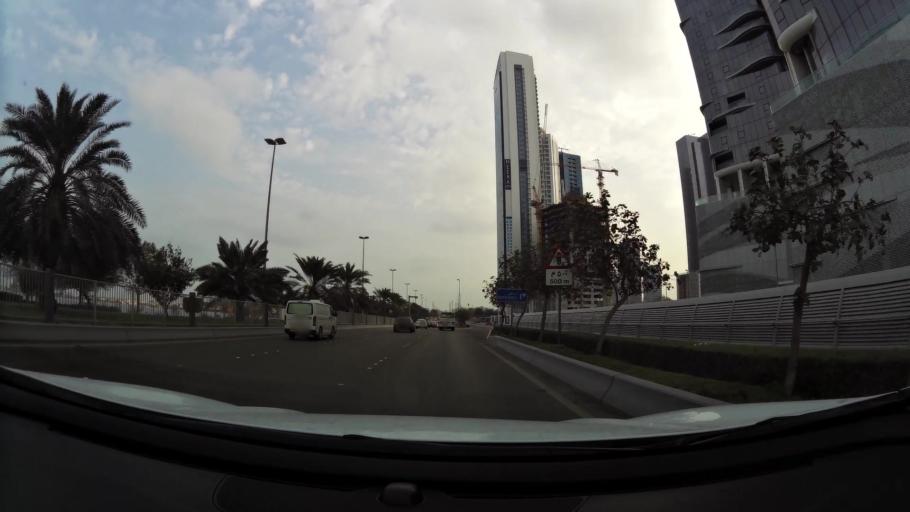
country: AE
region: Abu Dhabi
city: Abu Dhabi
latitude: 24.5023
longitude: 54.3670
